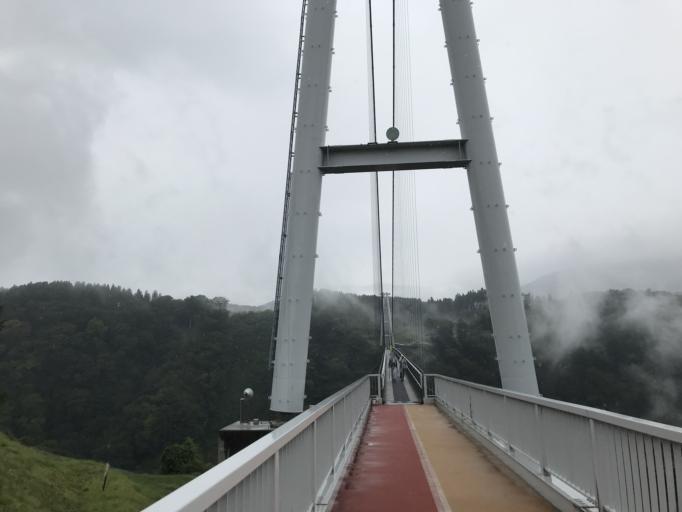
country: JP
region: Oita
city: Tsukawaki
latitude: 33.1725
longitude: 131.2252
